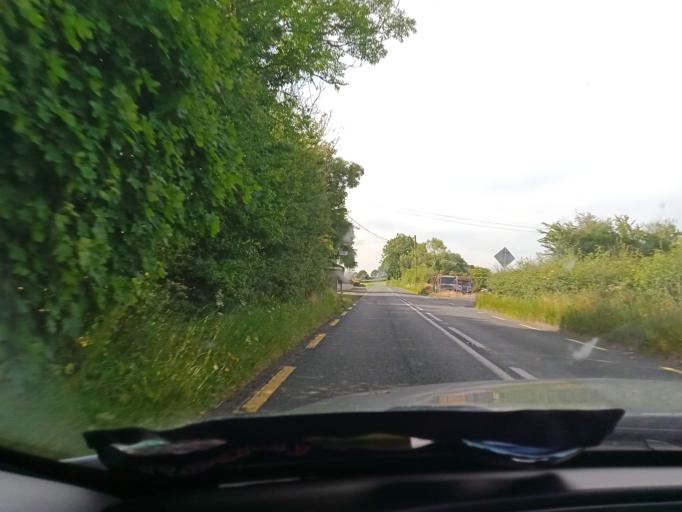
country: IE
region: Leinster
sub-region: An Longfort
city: Granard
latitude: 53.8844
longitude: -7.4398
